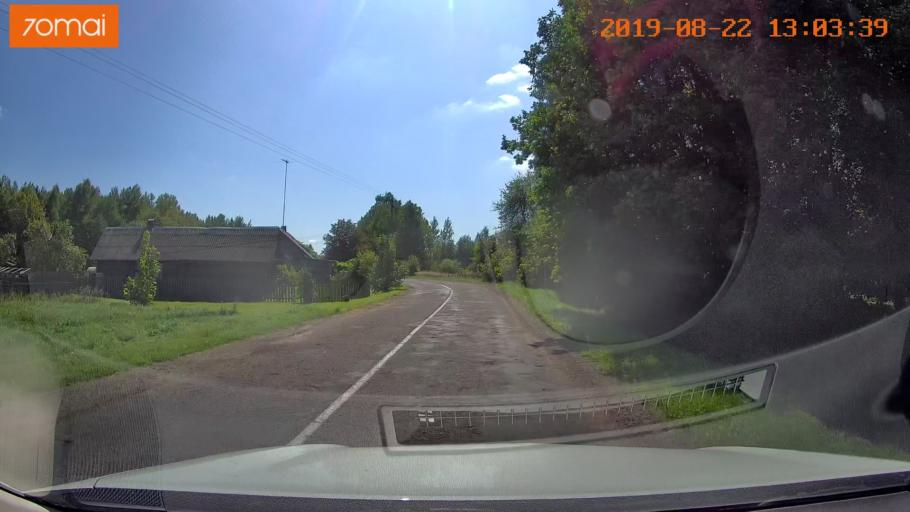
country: BY
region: Minsk
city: Prawdzinski
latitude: 53.3784
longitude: 27.8211
